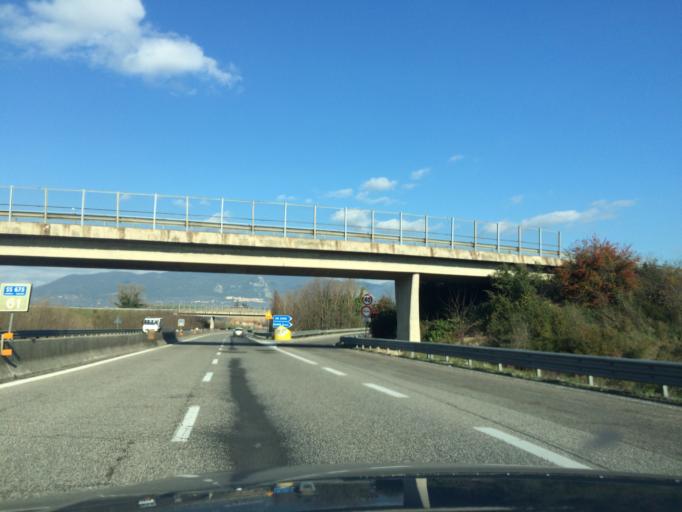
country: IT
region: Umbria
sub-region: Provincia di Terni
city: Narni Scalo
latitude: 42.5564
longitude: 12.5358
